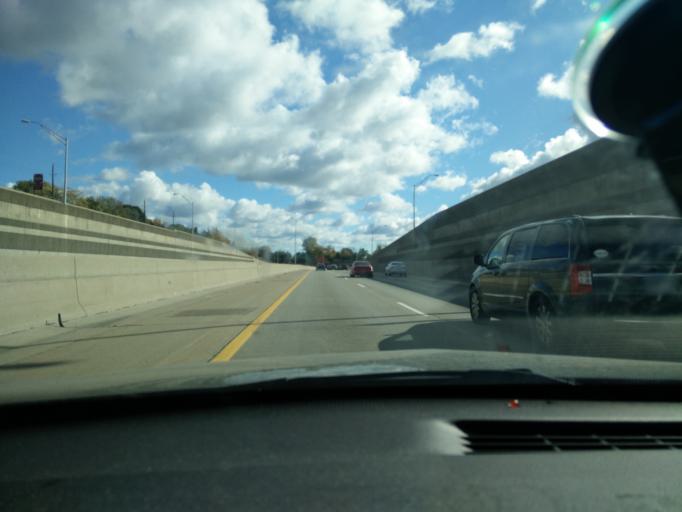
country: US
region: Michigan
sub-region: Oakland County
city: Lathrup Village
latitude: 42.4877
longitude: -83.2176
